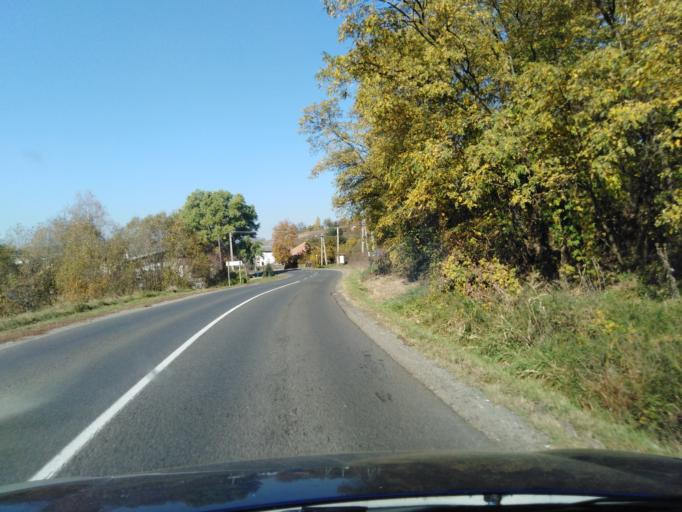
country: HU
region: Nograd
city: Karancslapujto
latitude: 48.1249
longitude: 19.7679
